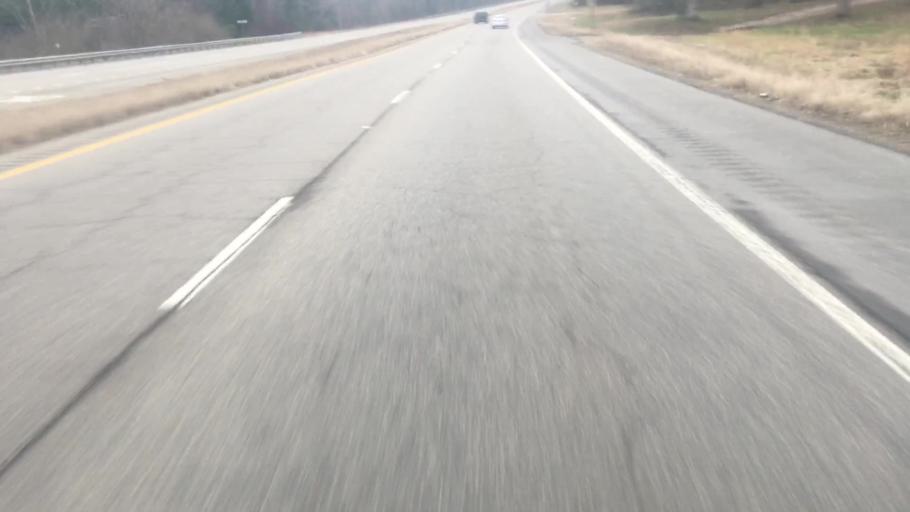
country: US
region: Alabama
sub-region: Walker County
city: Cordova
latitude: 33.8186
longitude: -87.1518
